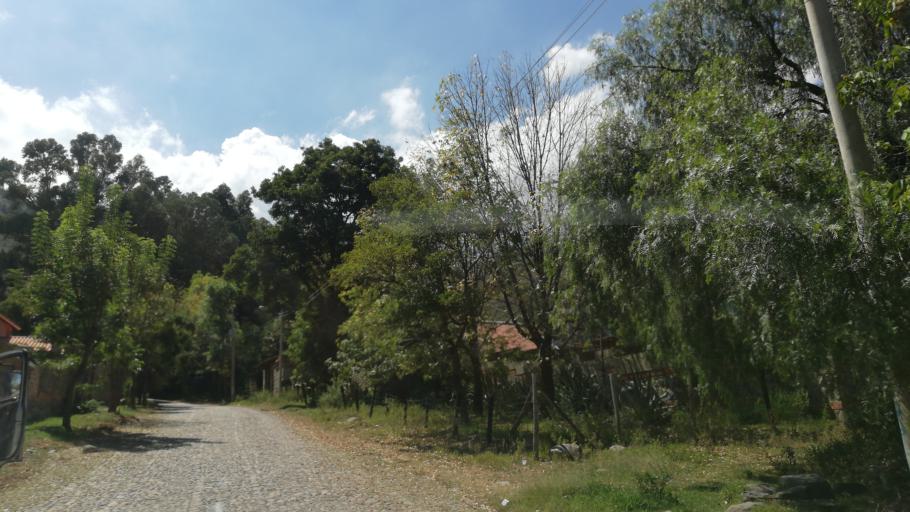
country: BO
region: Cochabamba
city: Cochabamba
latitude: -17.3225
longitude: -66.2126
